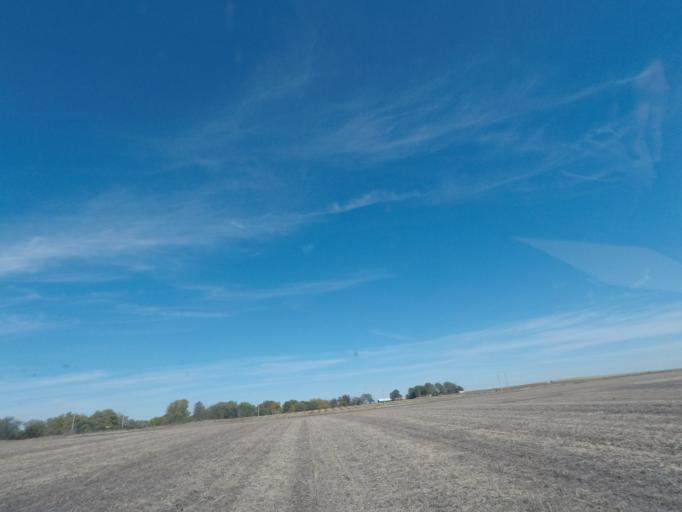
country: US
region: Iowa
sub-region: Story County
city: Nevada
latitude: 42.0400
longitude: -93.3611
